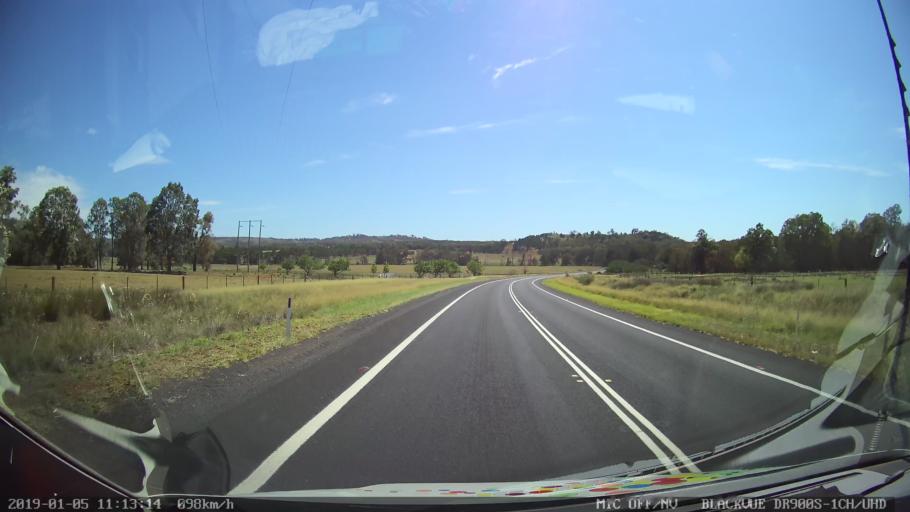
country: AU
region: New South Wales
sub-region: Warrumbungle Shire
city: Coonabarabran
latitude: -31.3726
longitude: 149.2682
